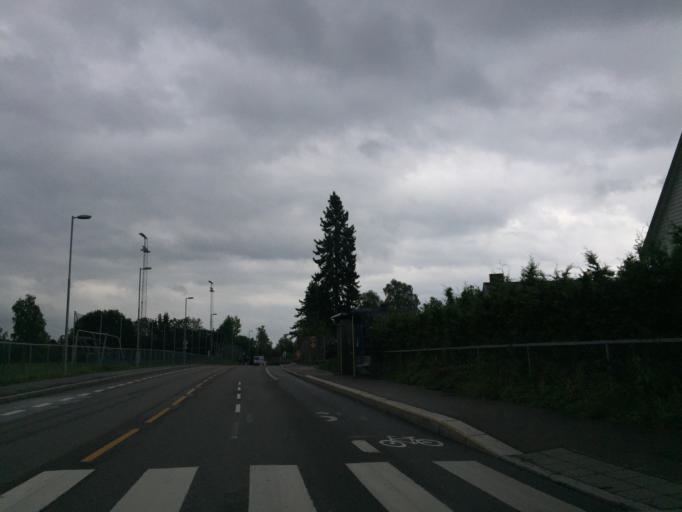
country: NO
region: Oslo
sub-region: Oslo
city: Sjolyststranda
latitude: 59.9508
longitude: 10.6751
